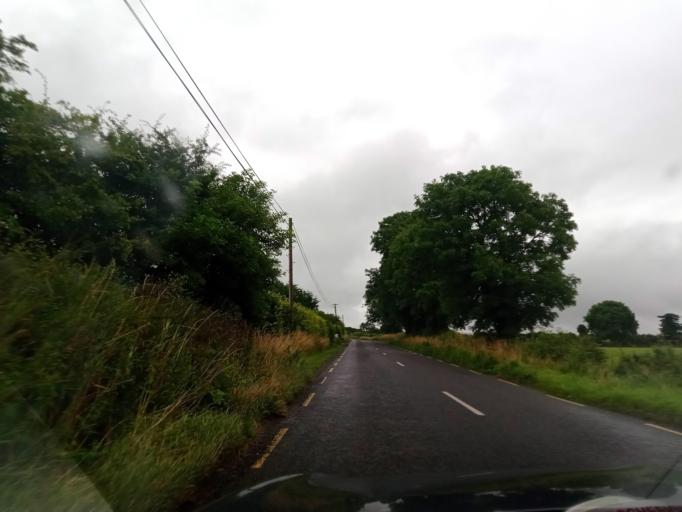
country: IE
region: Leinster
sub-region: Laois
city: Abbeyleix
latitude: 52.9102
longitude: -7.3035
